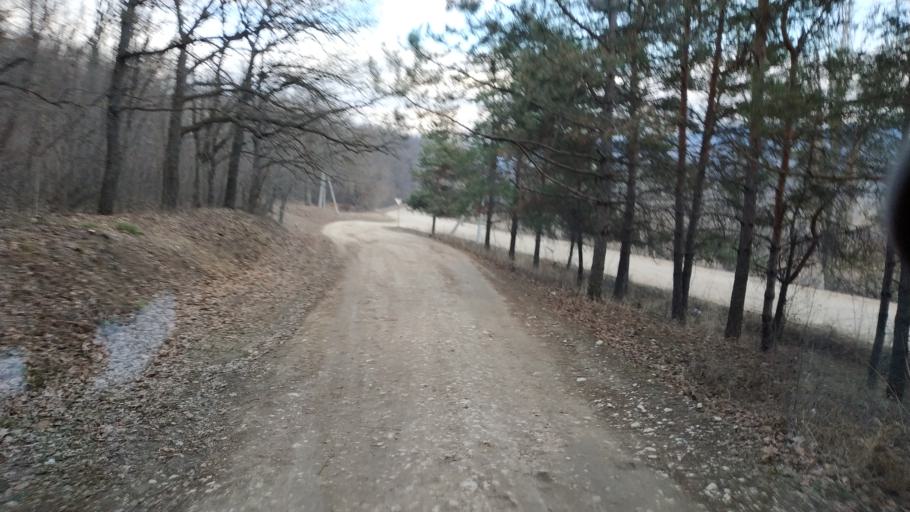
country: MD
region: Calarasi
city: Calarasi
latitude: 47.3324
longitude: 28.2196
